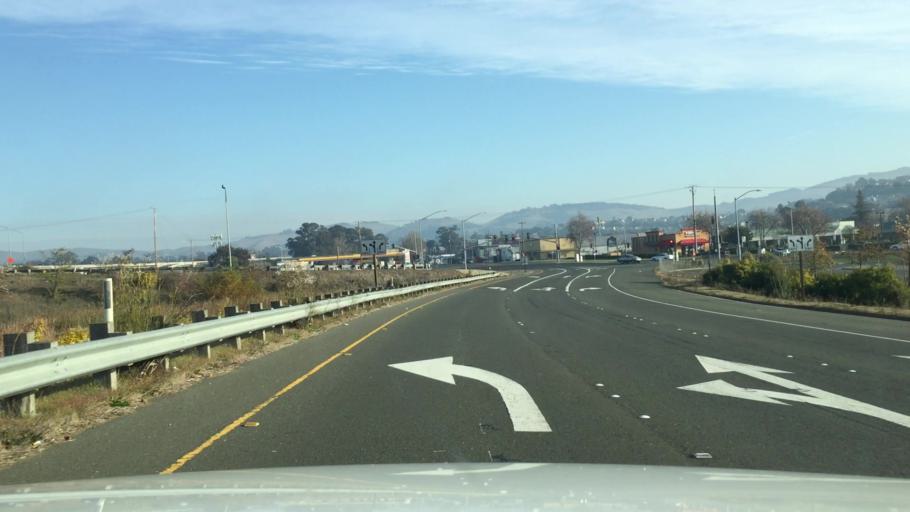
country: US
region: California
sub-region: Solano County
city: Vallejo
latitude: 38.1366
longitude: -122.2580
